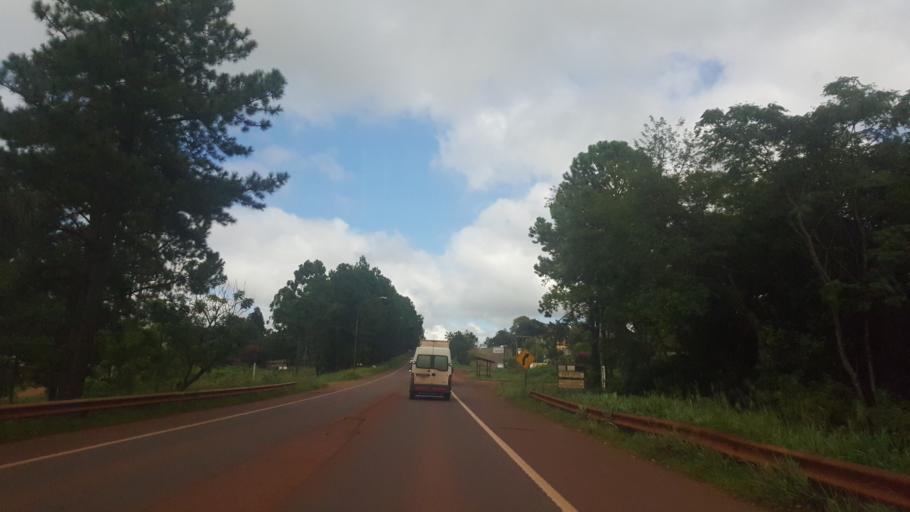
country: AR
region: Misiones
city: Aristobulo del Valle
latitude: -27.0845
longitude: -54.8244
